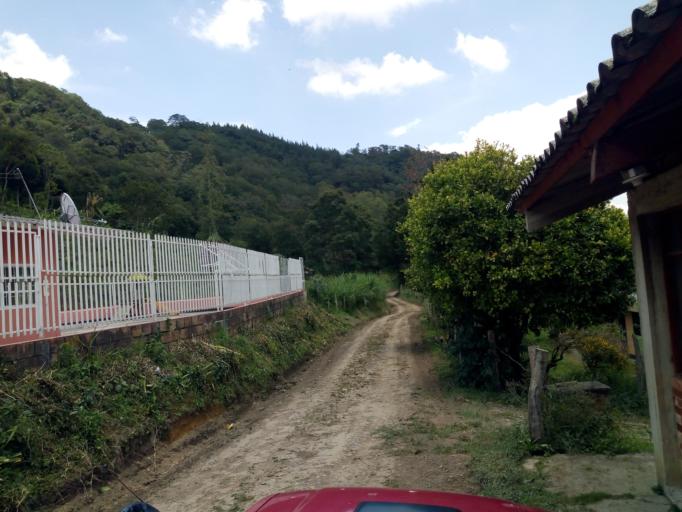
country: CO
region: Boyaca
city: Moniquira
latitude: 5.8658
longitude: -73.5160
